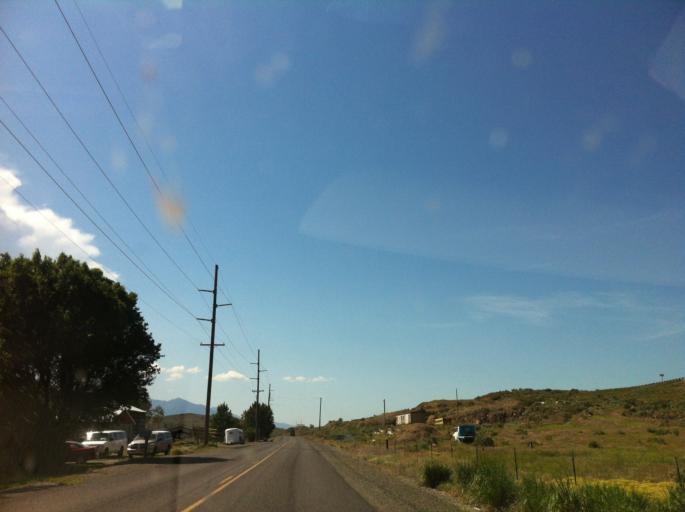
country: US
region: Oregon
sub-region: Baker County
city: Baker City
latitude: 44.7165
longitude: -117.7740
